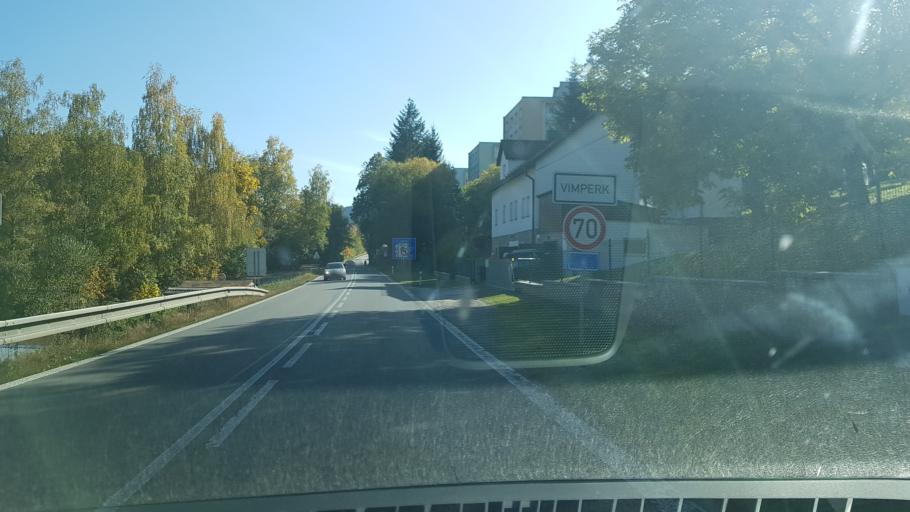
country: CZ
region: Jihocesky
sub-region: Okres Prachatice
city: Vimperk
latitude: 49.0633
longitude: 13.7820
